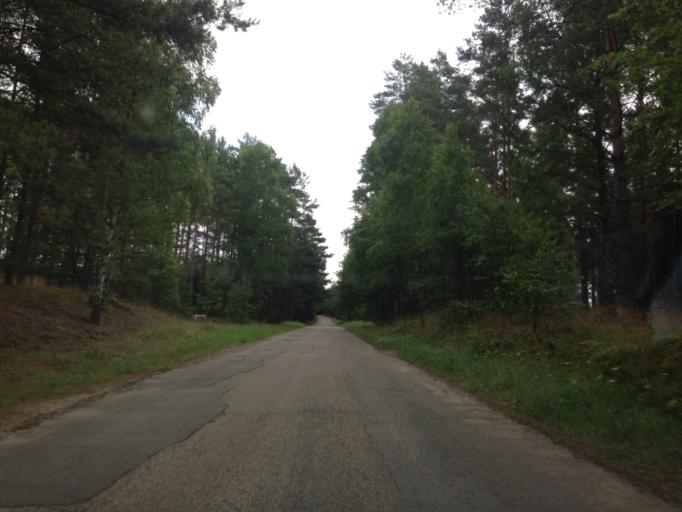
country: PL
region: Pomeranian Voivodeship
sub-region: Powiat koscierski
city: Lipusz
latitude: 54.0727
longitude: 17.7402
